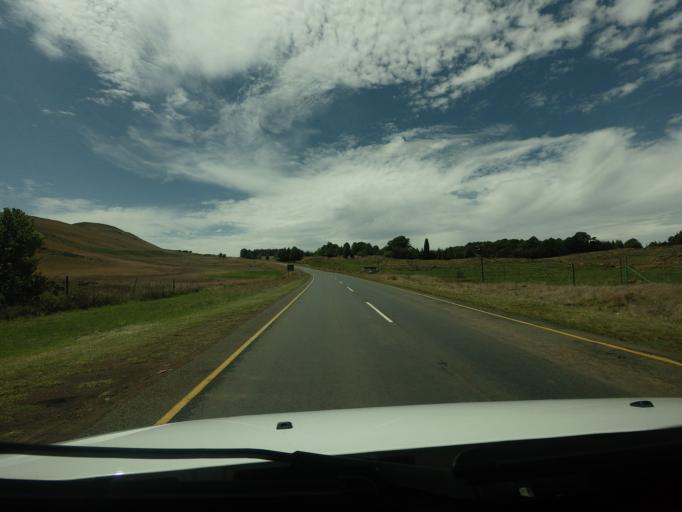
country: ZA
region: Mpumalanga
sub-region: Nkangala District Municipality
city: Belfast
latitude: -25.4118
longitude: 30.1151
